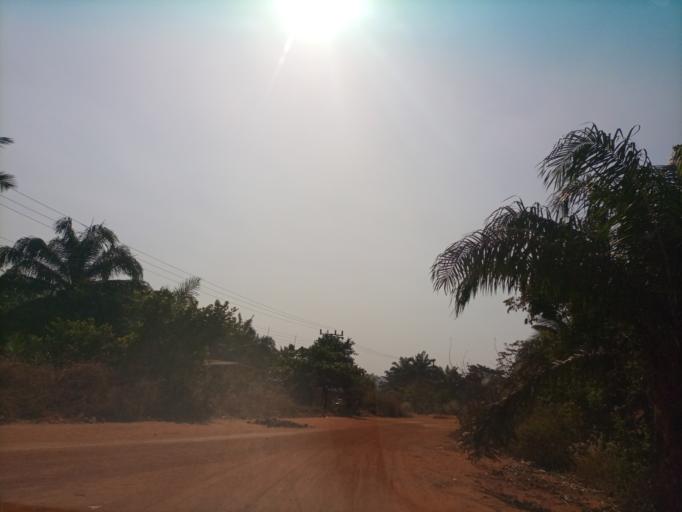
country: NG
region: Enugu
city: Aku
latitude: 6.7078
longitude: 7.3364
